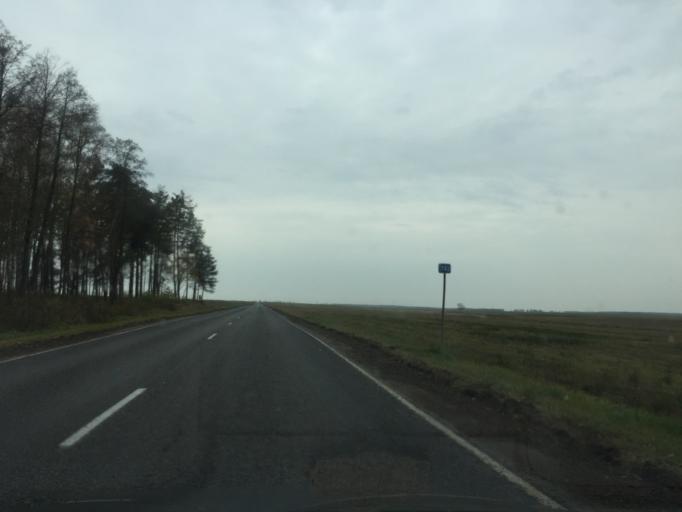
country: BY
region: Gomel
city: Dowsk
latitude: 53.1875
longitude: 30.5038
